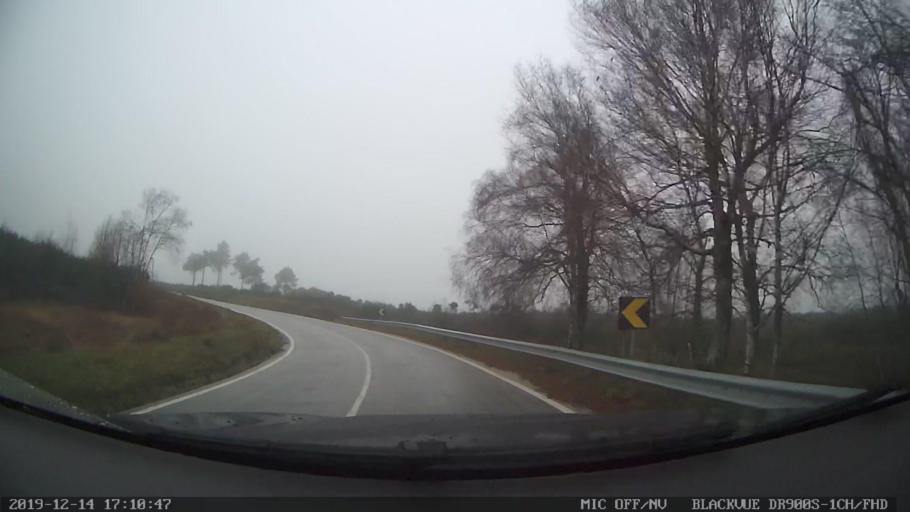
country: PT
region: Vila Real
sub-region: Vila Pouca de Aguiar
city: Vila Pouca de Aguiar
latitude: 41.4829
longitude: -7.6107
